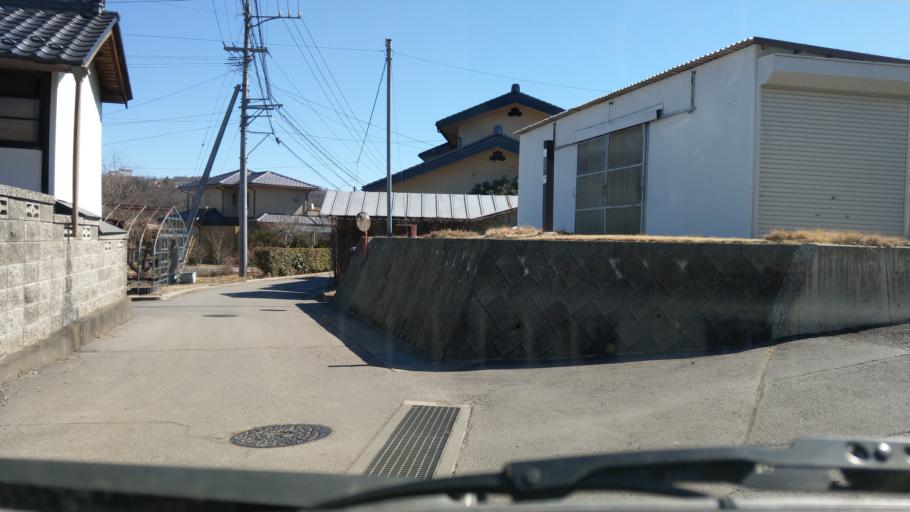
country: JP
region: Nagano
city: Komoro
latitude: 36.3297
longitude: 138.4032
